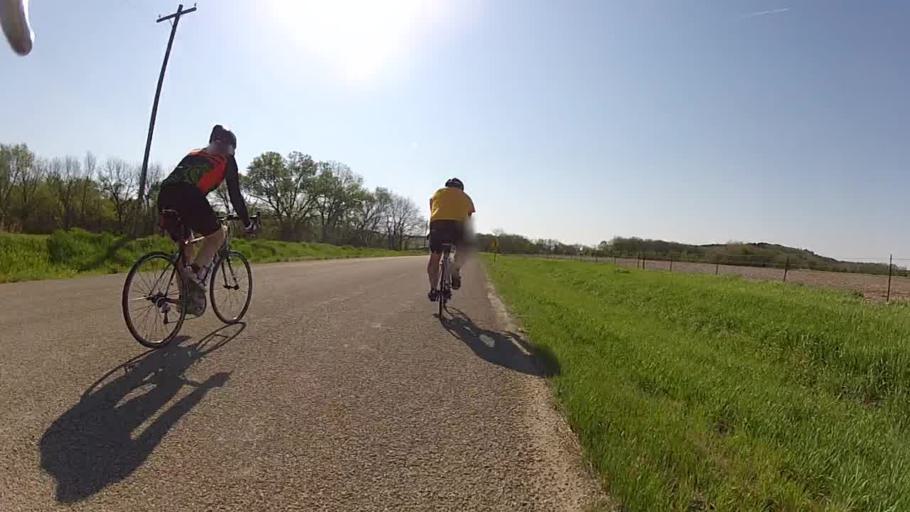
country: US
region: Kansas
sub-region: Geary County
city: Grandview Plaza
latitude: 39.0502
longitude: -96.7352
